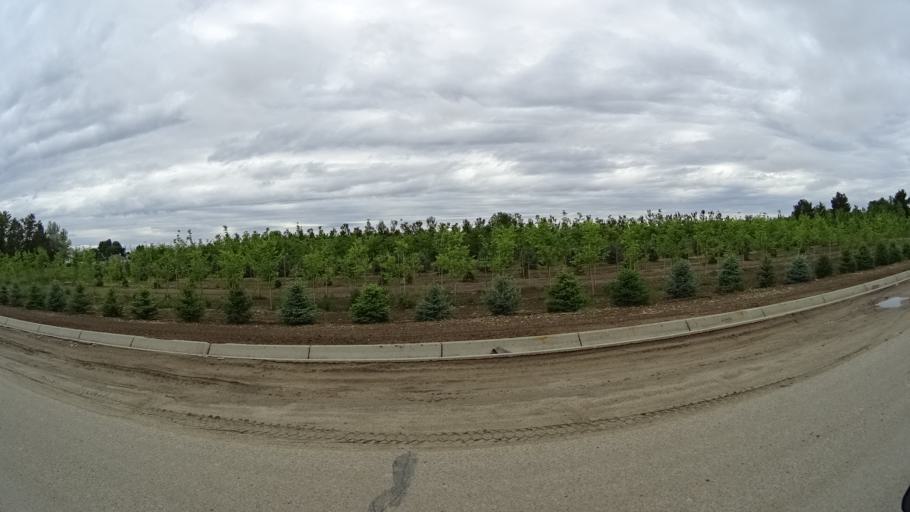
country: US
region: Idaho
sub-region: Ada County
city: Eagle
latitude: 43.7296
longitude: -116.3794
